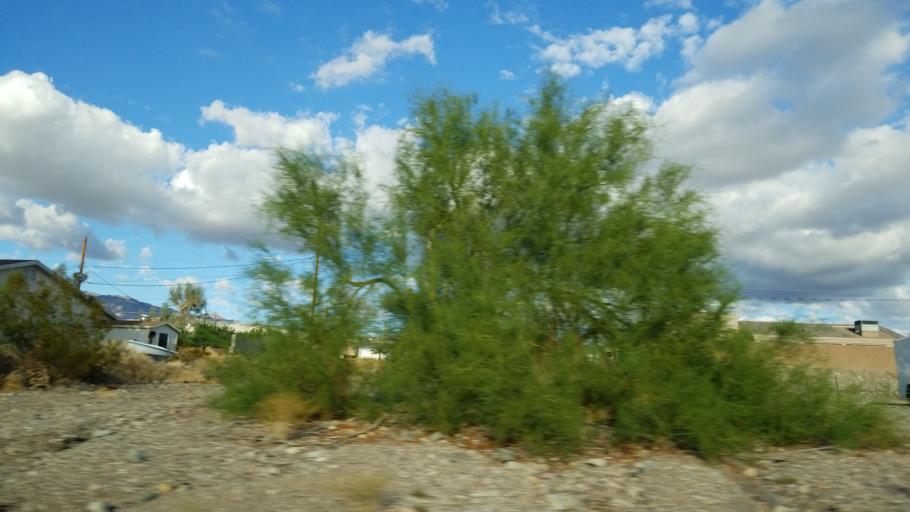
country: US
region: Arizona
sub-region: Mohave County
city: Lake Havasu City
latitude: 34.4639
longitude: -114.2607
